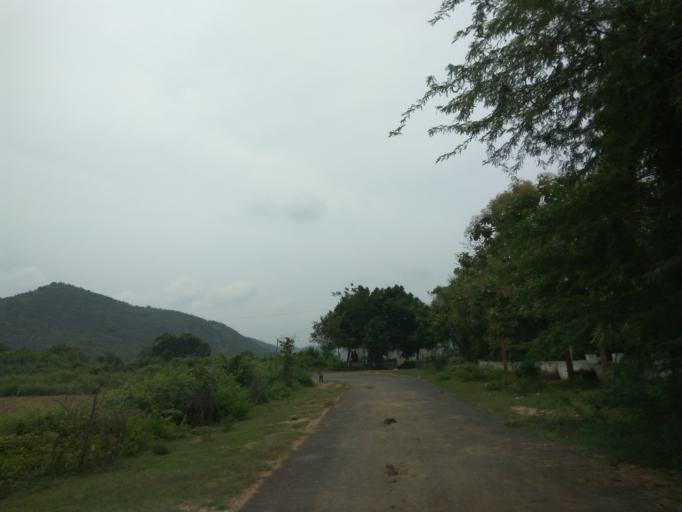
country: IN
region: Andhra Pradesh
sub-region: Prakasam
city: Cumbum
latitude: 15.4454
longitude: 79.0799
